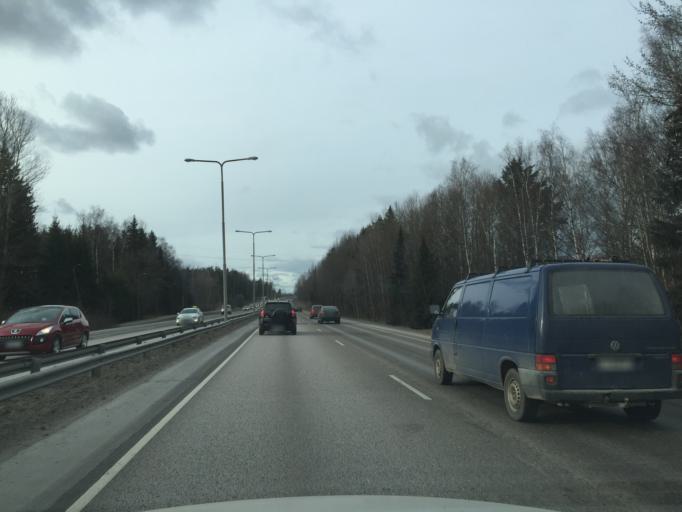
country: FI
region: Uusimaa
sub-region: Helsinki
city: Teekkarikylae
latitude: 60.2543
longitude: 24.8823
